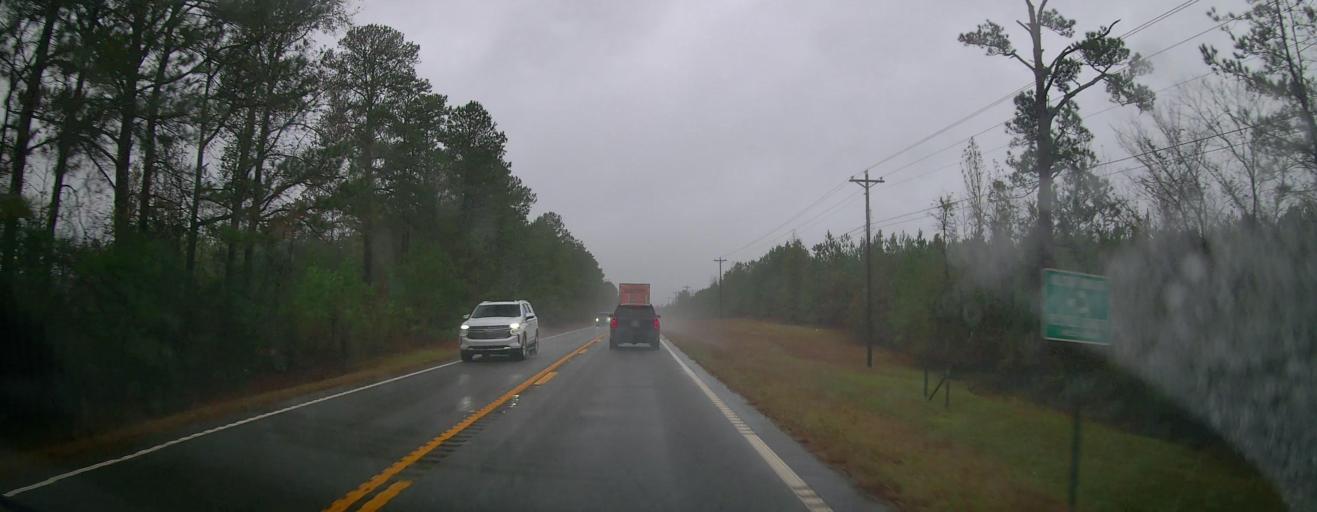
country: US
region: Georgia
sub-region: Jones County
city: Gray
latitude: 33.0865
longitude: -83.4839
